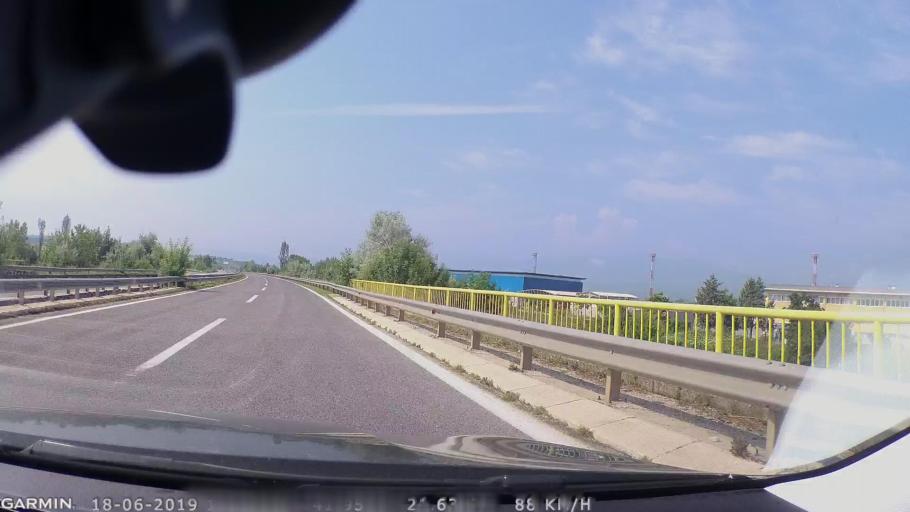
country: MK
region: Petrovec
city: Petrovec
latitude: 41.9552
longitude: 21.6307
